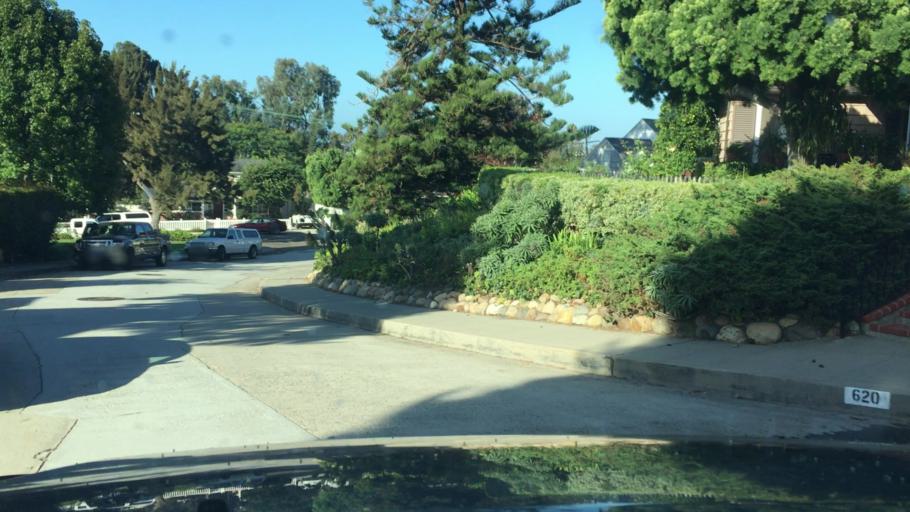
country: US
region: California
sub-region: San Diego County
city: La Jolla
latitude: 32.8235
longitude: -117.2729
